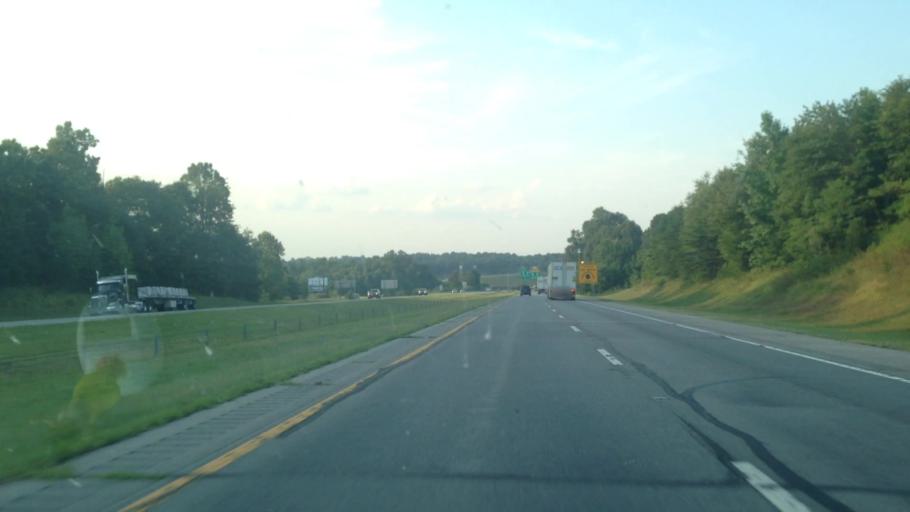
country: US
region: Virginia
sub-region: City of Danville
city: Danville
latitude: 36.5313
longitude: -79.4702
